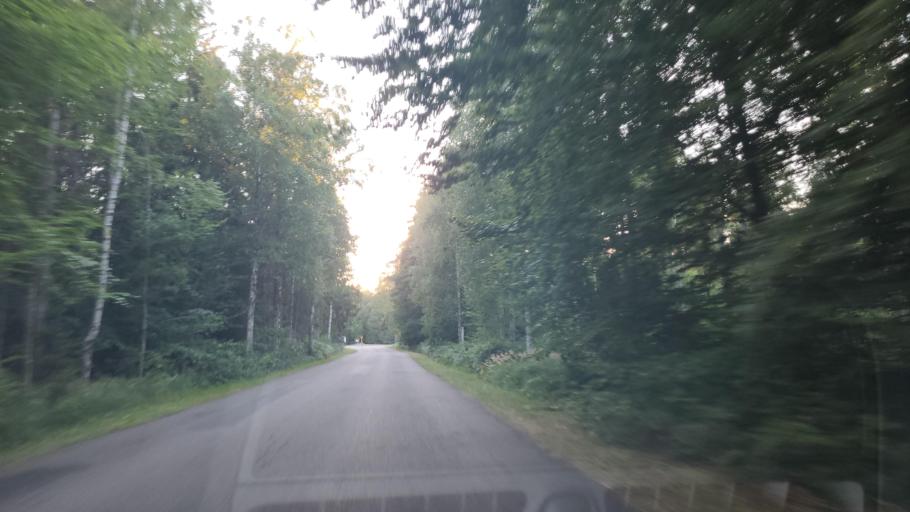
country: SE
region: Kalmar
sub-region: Borgholms Kommun
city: Borgholm
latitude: 57.2788
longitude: 17.0254
